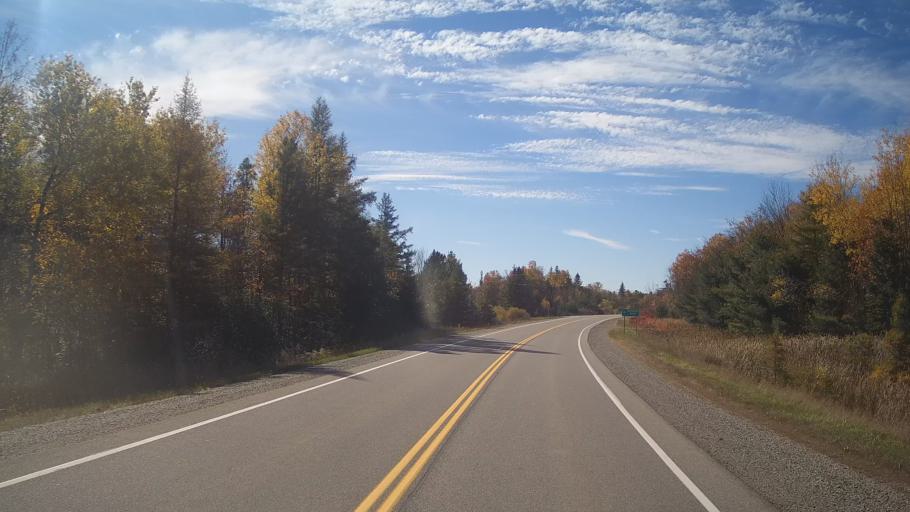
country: CA
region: Ontario
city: Perth
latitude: 44.8057
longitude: -76.6463
